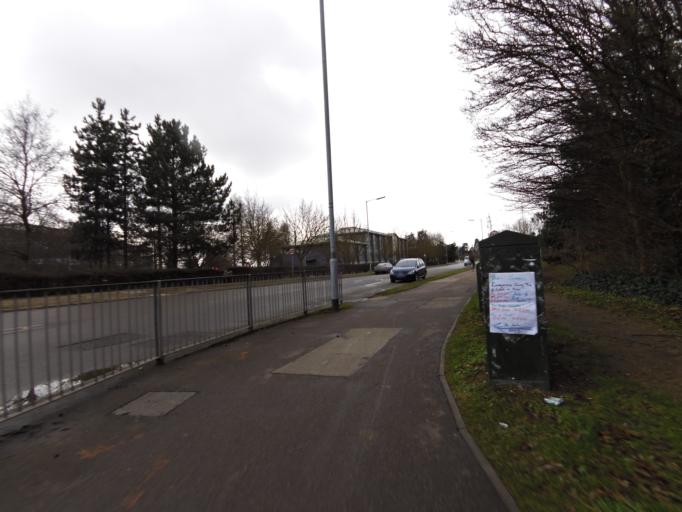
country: GB
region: England
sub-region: Cambridgeshire
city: Cambridge
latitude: 52.2313
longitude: 0.1506
